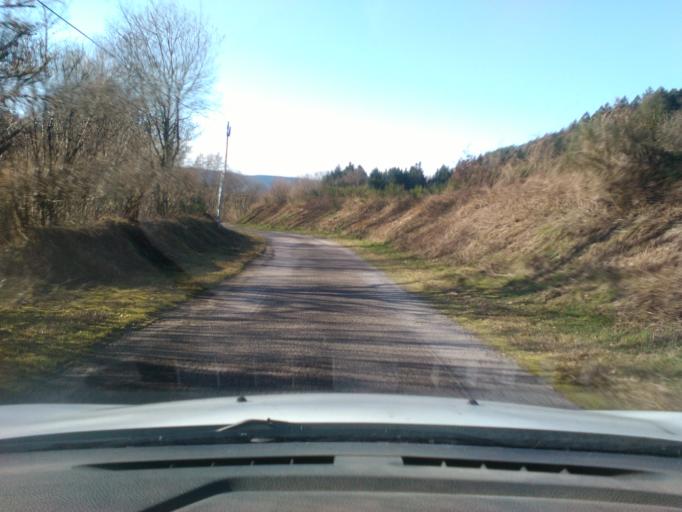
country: FR
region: Lorraine
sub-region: Departement des Vosges
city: Vecoux
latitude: 47.9720
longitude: 6.6654
